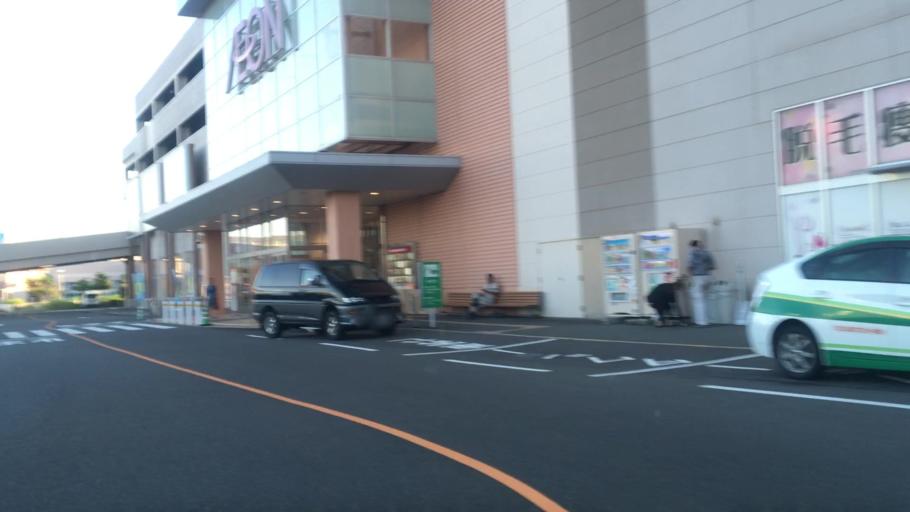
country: JP
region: Tottori
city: Tottori
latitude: 35.5235
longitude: 134.2015
